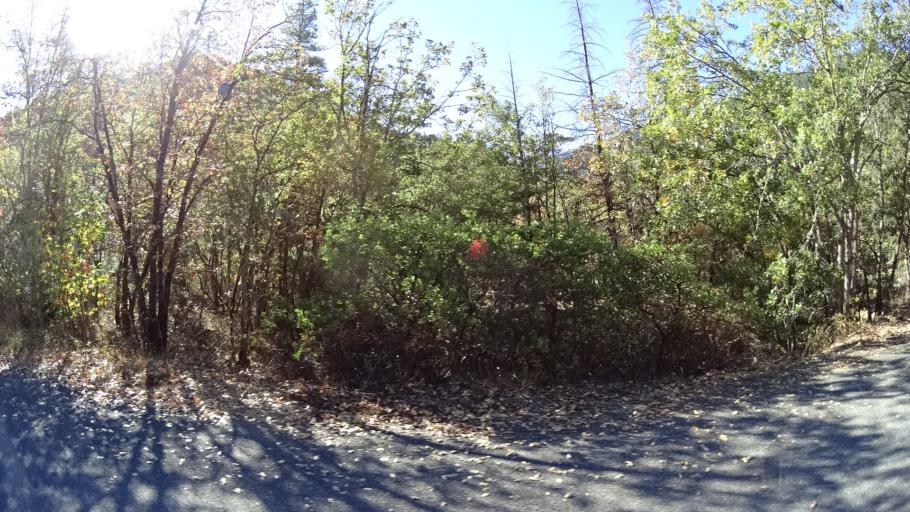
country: US
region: California
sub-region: Humboldt County
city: Willow Creek
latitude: 41.1884
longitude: -123.2145
